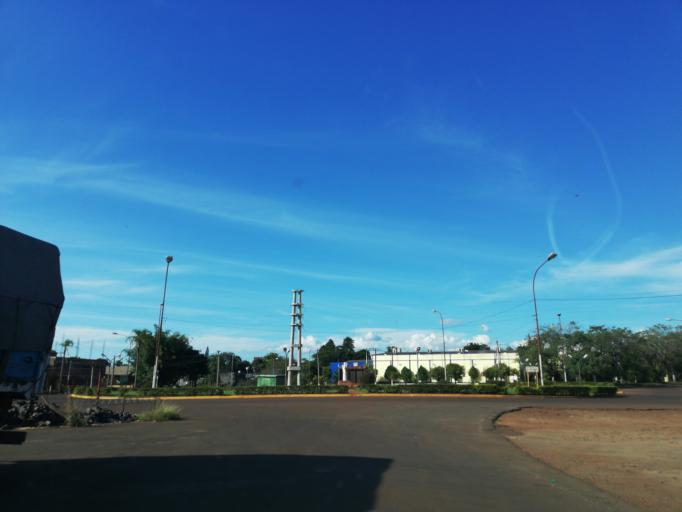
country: AR
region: Misiones
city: Dos de Mayo
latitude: -27.0001
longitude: -54.4941
